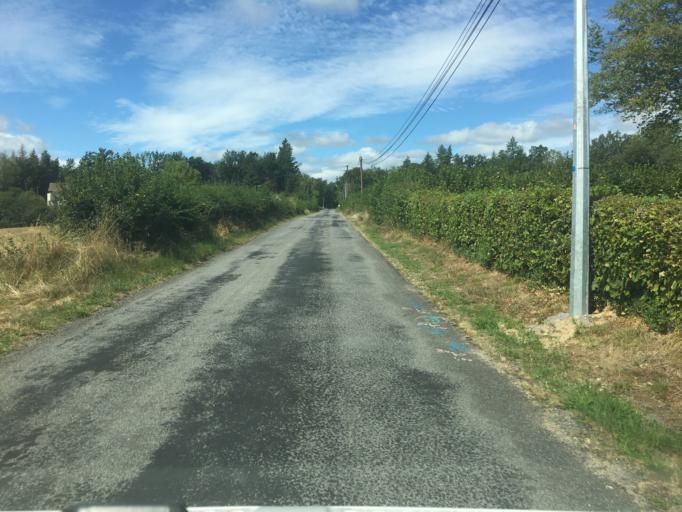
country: FR
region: Auvergne
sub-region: Departement du Cantal
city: Champagnac
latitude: 45.4248
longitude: 2.3736
